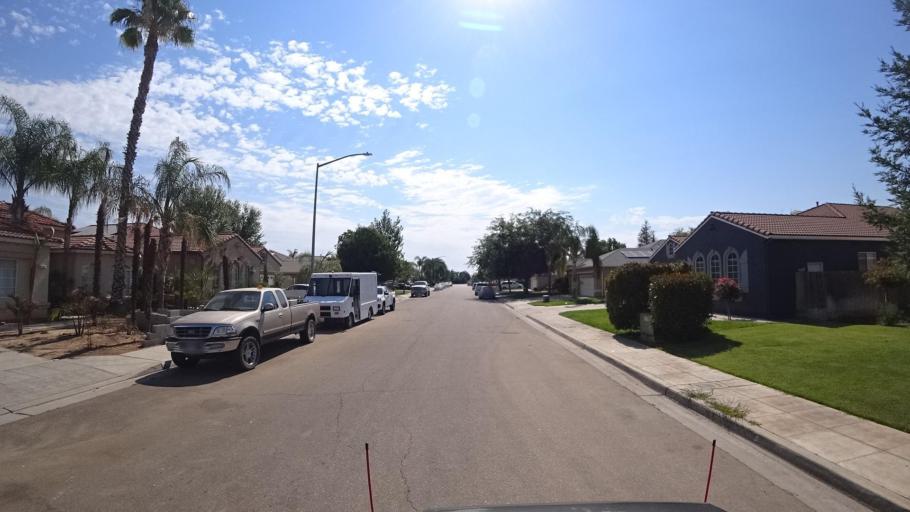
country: US
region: California
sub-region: Fresno County
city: Sunnyside
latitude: 36.7186
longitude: -119.6937
